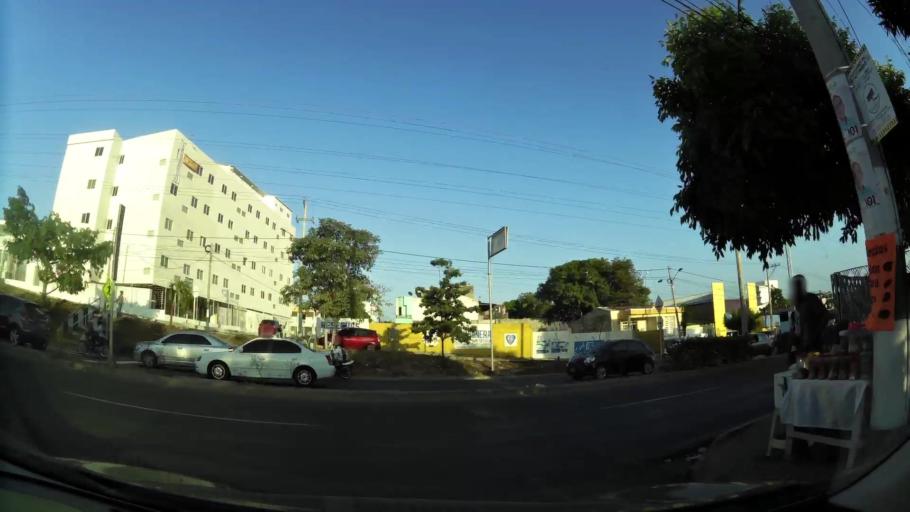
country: CO
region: Bolivar
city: Cartagena
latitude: 10.3933
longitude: -75.5169
